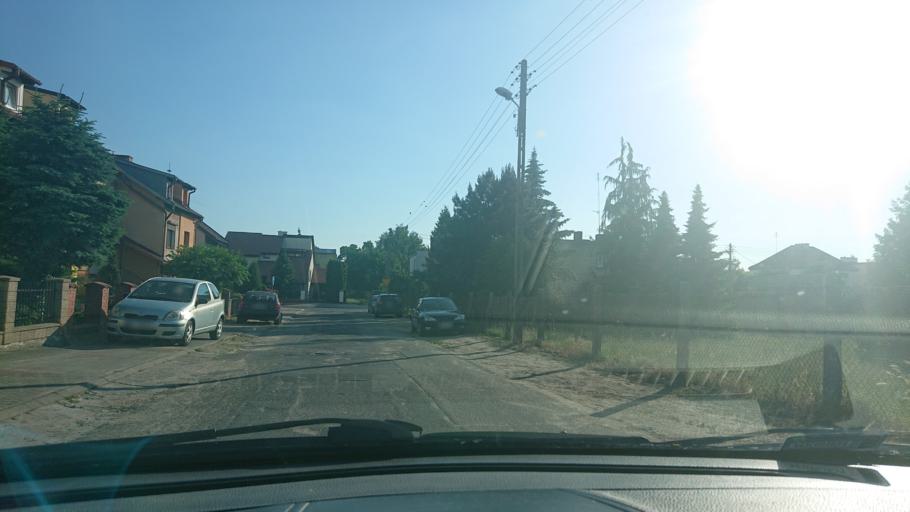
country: PL
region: Greater Poland Voivodeship
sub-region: Powiat gnieznienski
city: Gniezno
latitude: 52.5209
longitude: 17.6103
